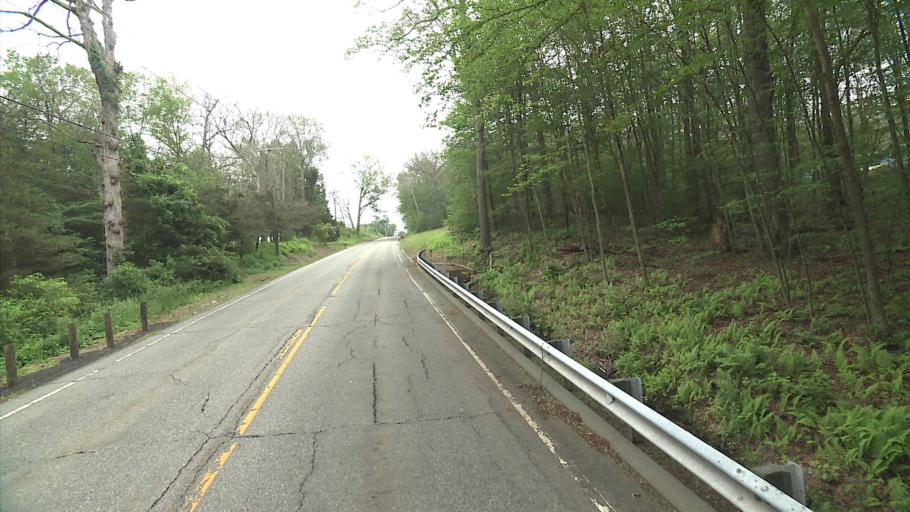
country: US
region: Connecticut
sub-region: Hartford County
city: Terramuggus
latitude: 41.6925
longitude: -72.4441
